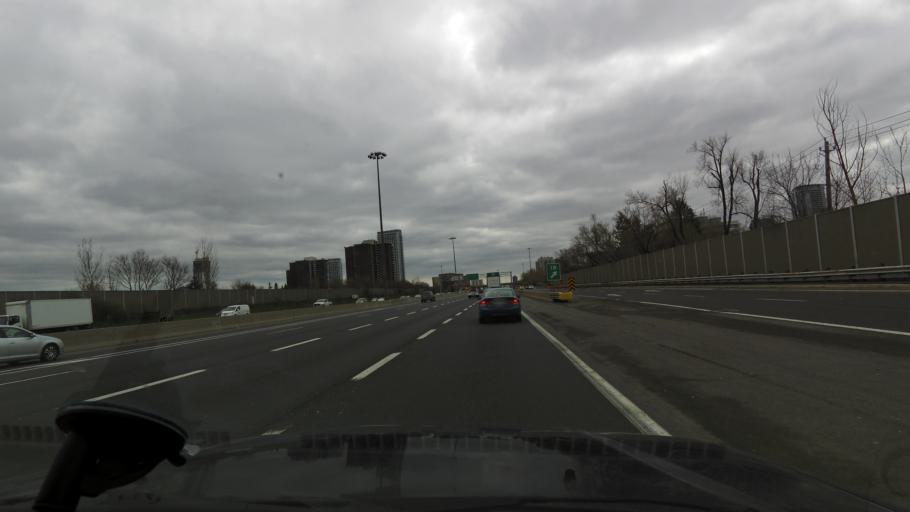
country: CA
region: Ontario
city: Willowdale
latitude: 43.7822
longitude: -79.3412
